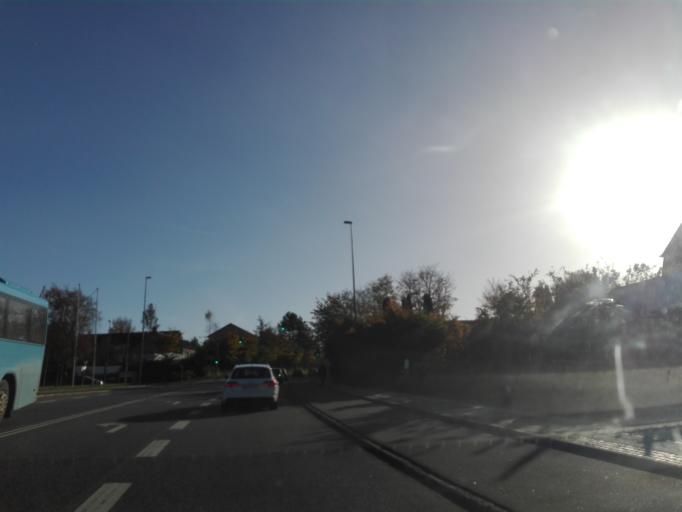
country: DK
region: Central Jutland
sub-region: Arhus Kommune
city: Arhus
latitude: 56.1130
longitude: 10.2089
